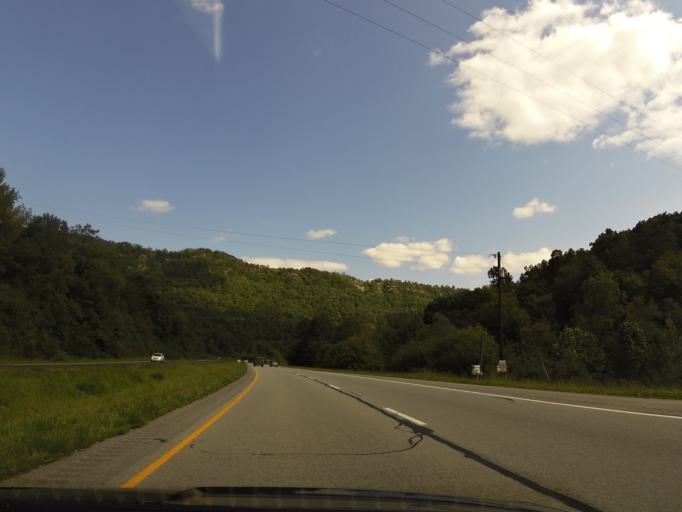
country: US
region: Kentucky
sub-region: Bell County
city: Pineville
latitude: 36.6971
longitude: -83.6900
